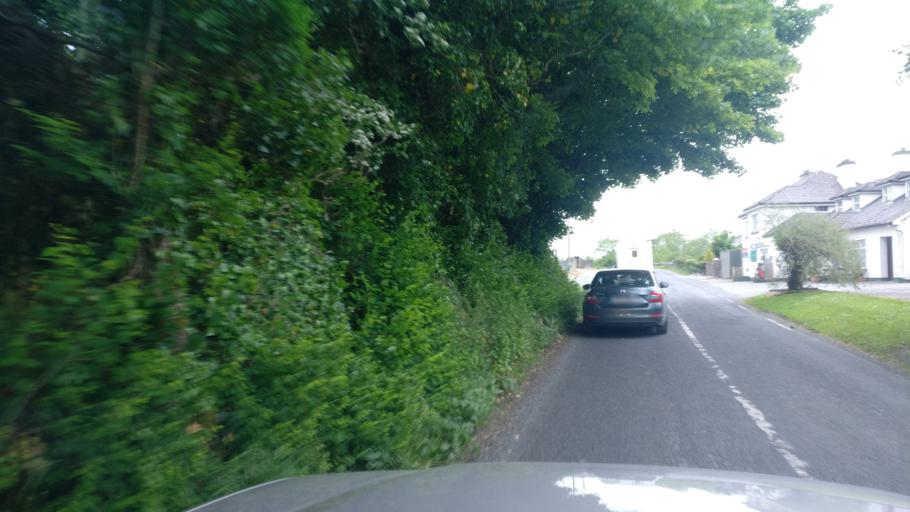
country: IE
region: Connaught
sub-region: County Galway
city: Portumna
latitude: 53.1199
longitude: -8.3167
